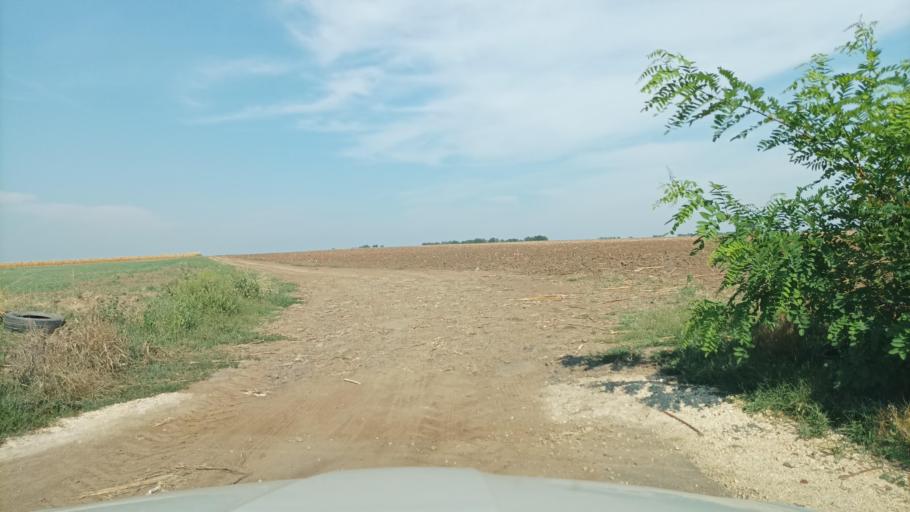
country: HU
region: Pest
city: Vacszentlaszlo
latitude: 47.5799
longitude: 19.5549
